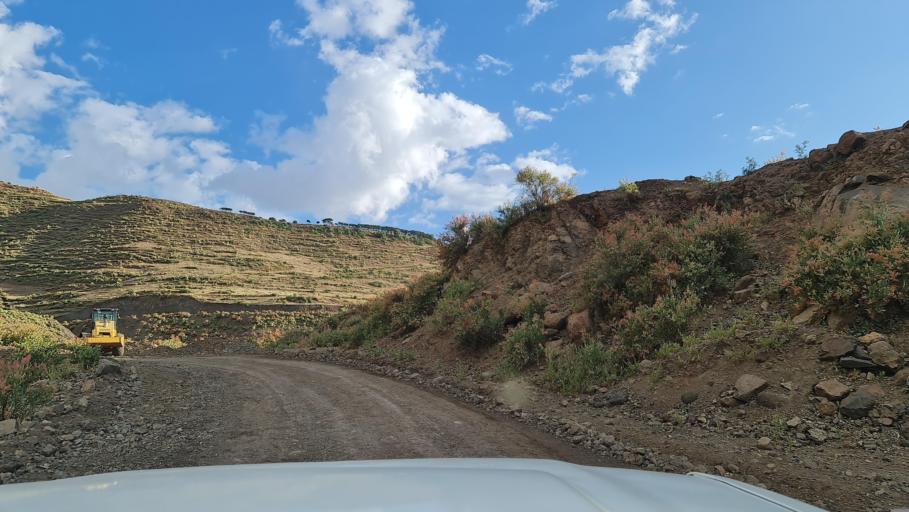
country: ET
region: Amhara
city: Debark'
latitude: 13.0503
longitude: 38.0196
